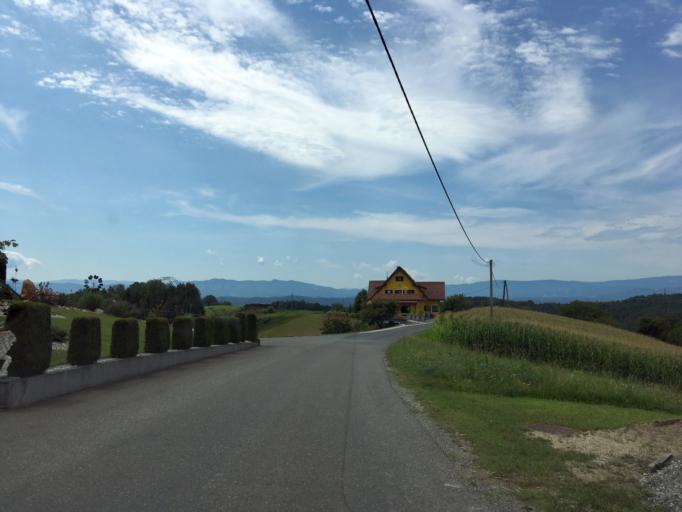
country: AT
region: Styria
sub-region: Politischer Bezirk Leibnitz
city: Kitzeck im Sausal
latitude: 46.7826
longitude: 15.4020
